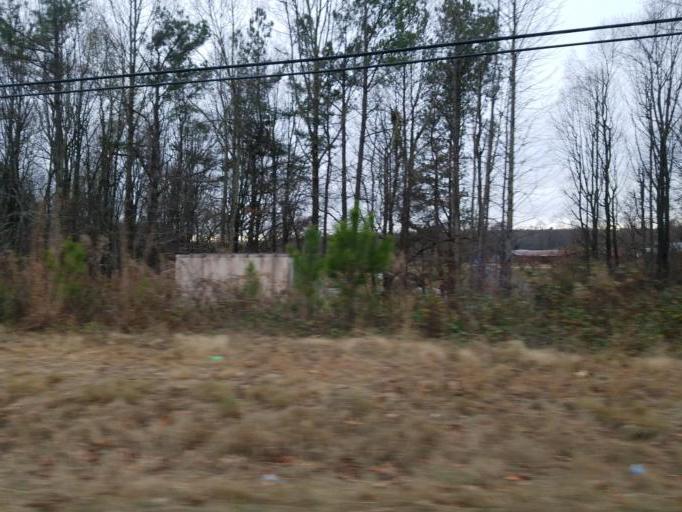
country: US
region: Georgia
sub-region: Dawson County
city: Dawsonville
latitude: 34.4820
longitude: -84.1642
